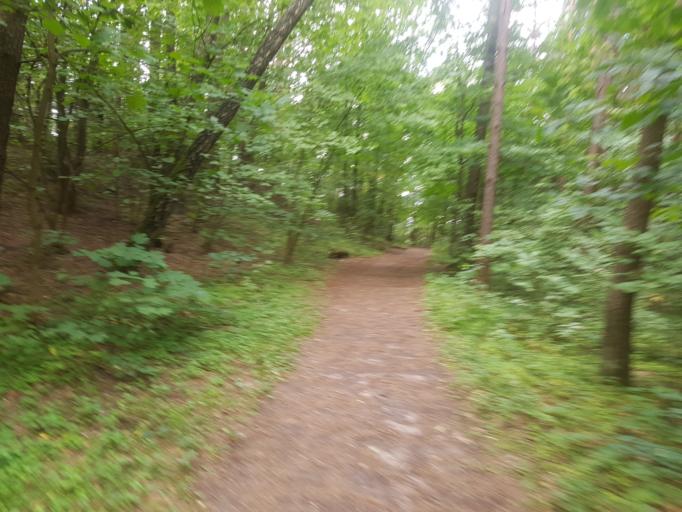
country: LT
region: Vilnius County
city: Rasos
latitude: 54.7837
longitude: 25.3382
